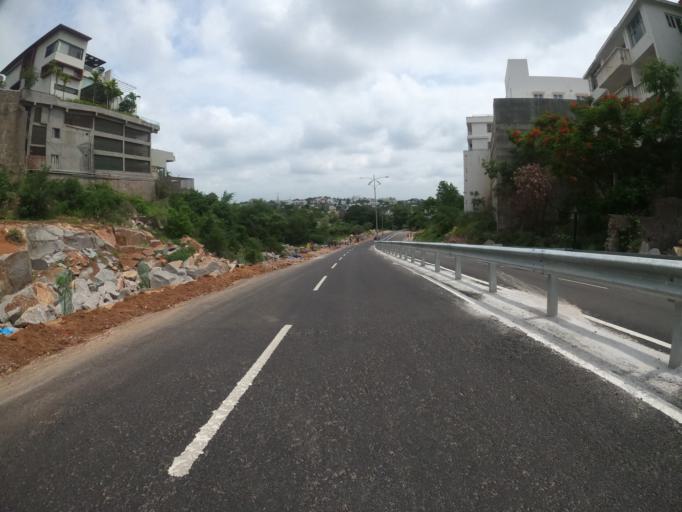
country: IN
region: Telangana
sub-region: Rangareddi
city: Kukatpalli
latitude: 17.4209
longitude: 78.3981
